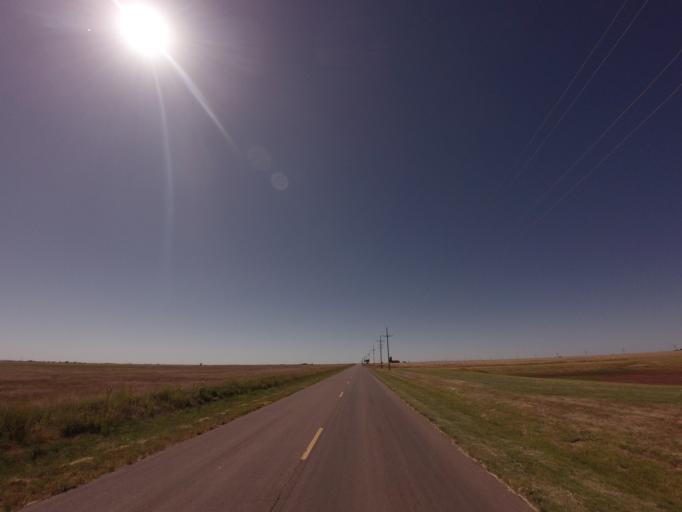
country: US
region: New Mexico
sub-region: Curry County
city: Clovis
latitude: 34.4484
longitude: -103.2162
